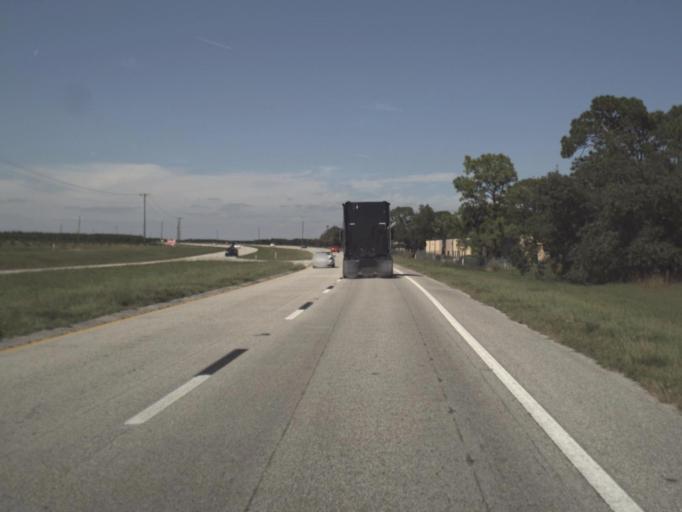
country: US
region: Florida
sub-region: Highlands County
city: Lake Placid
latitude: 27.3510
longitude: -81.3878
